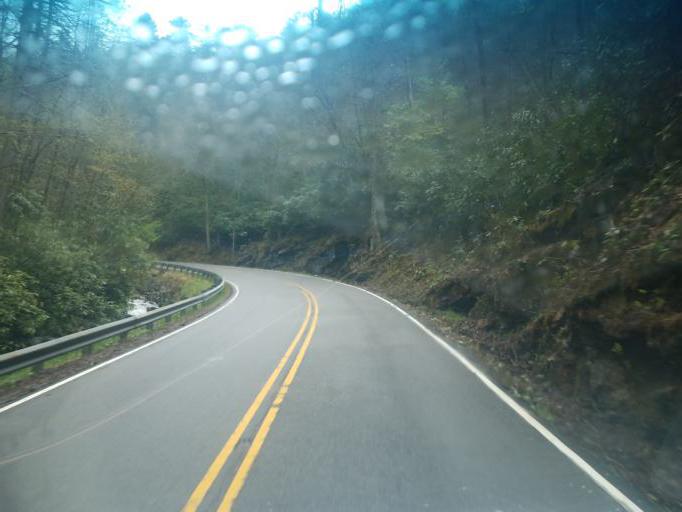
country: US
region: Virginia
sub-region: Washington County
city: Glade Spring
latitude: 36.6418
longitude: -81.7147
